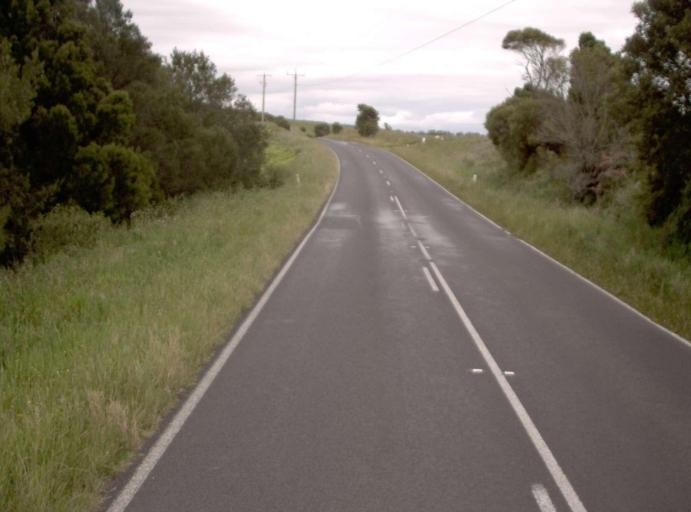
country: AU
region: Victoria
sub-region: Bass Coast
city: North Wonthaggi
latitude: -38.4554
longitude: 145.7948
